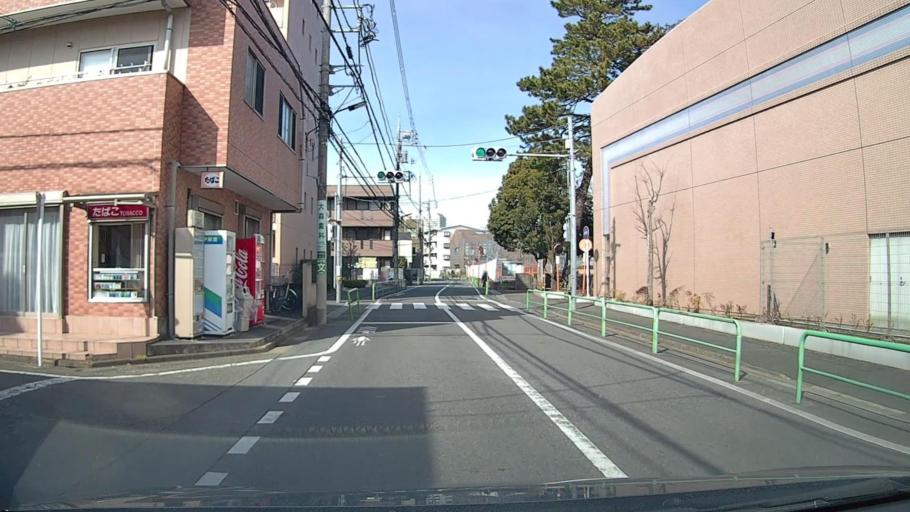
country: JP
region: Tokyo
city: Musashino
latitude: 35.7405
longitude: 139.5878
